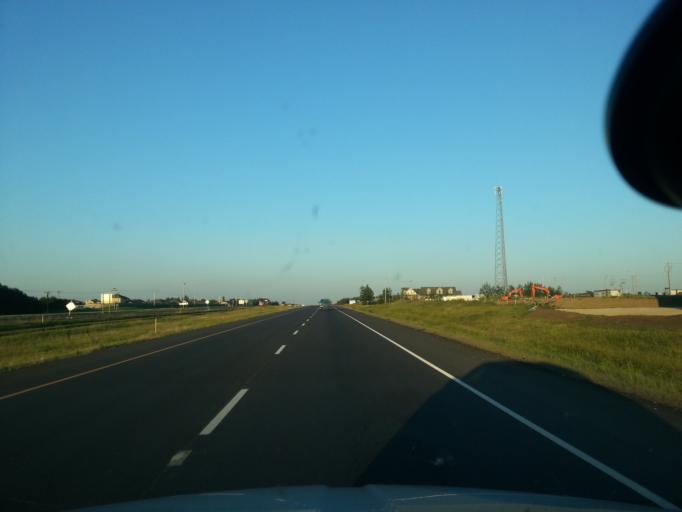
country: CA
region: Alberta
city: St. Albert
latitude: 53.5695
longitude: -113.7425
